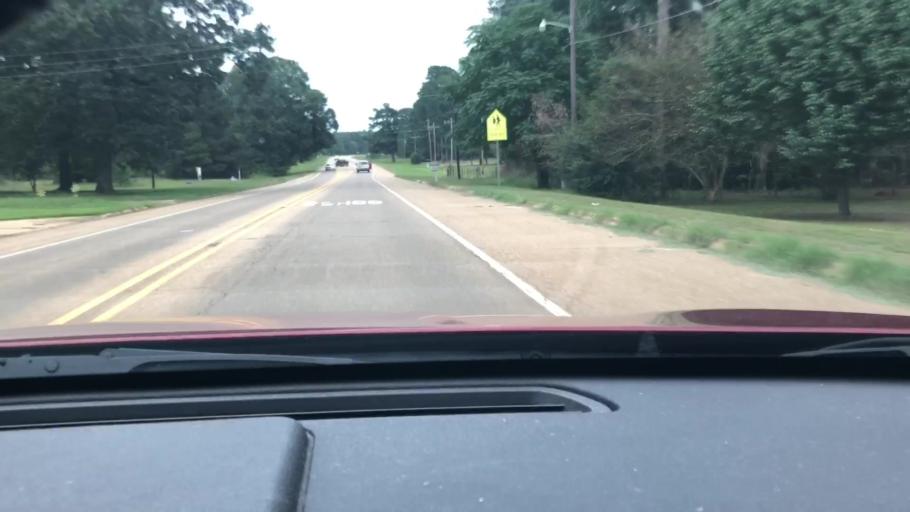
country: US
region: Arkansas
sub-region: Lafayette County
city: Stamps
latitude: 33.3650
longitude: -93.4822
